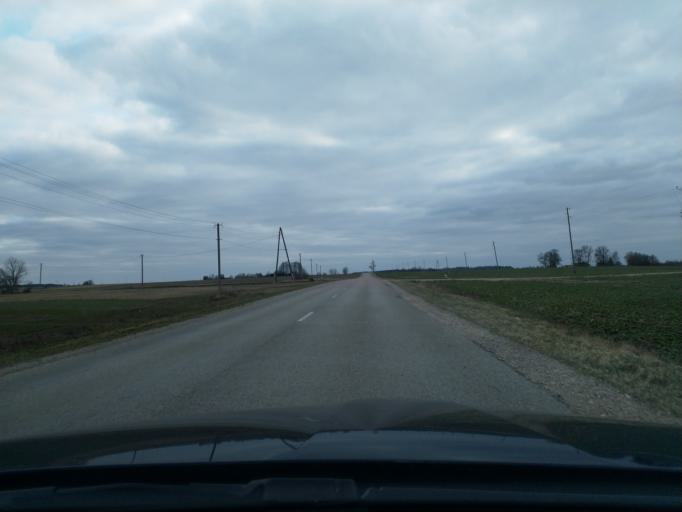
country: LV
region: Talsu Rajons
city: Sabile
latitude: 56.9564
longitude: 22.6115
